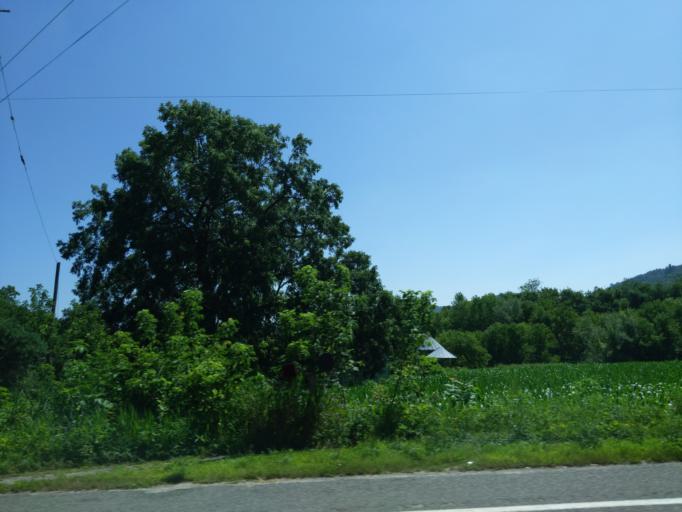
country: US
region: Wisconsin
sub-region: Vernon County
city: Westby
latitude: 43.6997
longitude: -91.0401
